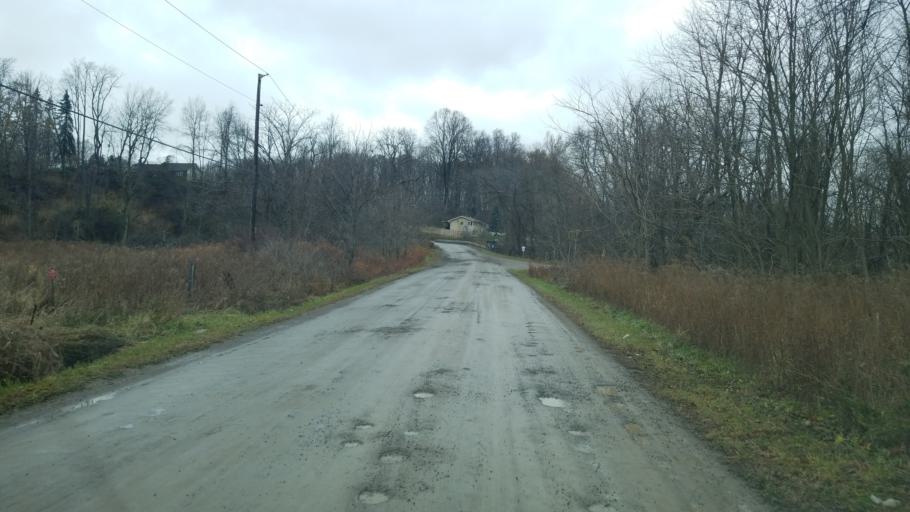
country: US
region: Ohio
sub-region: Ashtabula County
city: Conneaut
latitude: 41.9256
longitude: -80.6045
